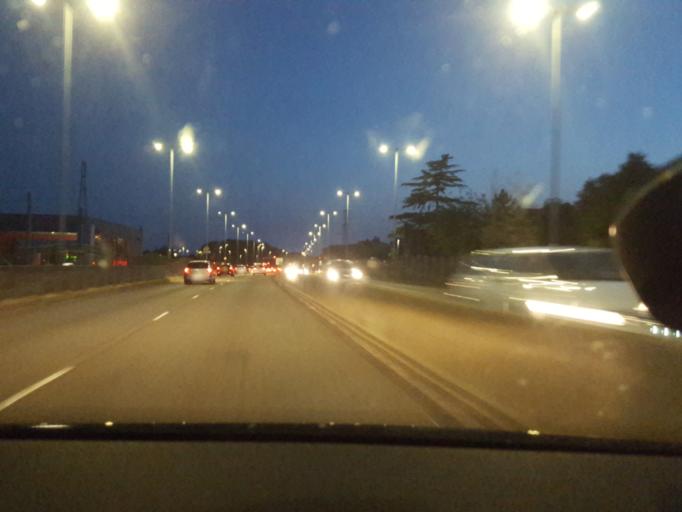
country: GB
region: England
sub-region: Leicestershire
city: Blaby
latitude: 52.6039
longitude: -1.1757
